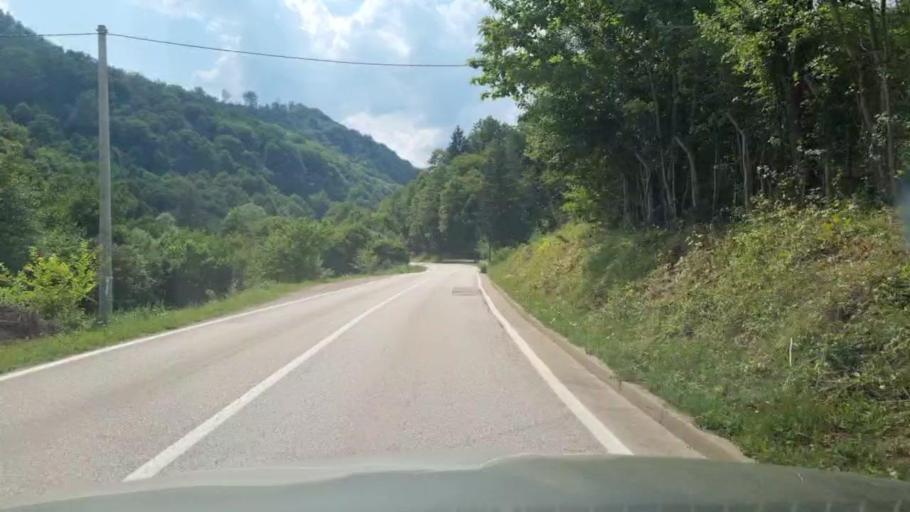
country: BA
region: Federation of Bosnia and Herzegovina
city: Kladanj
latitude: 44.2340
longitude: 18.7394
